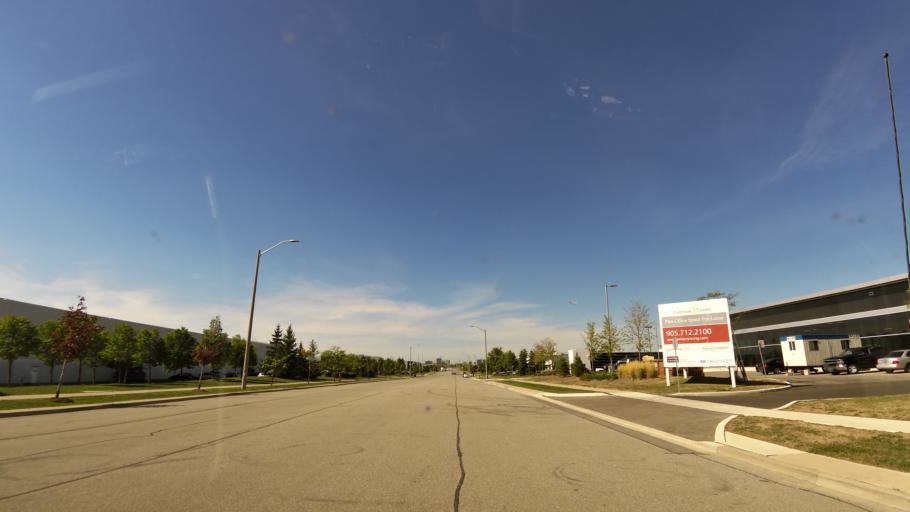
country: CA
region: Ontario
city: Mississauga
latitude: 43.6332
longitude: -79.6945
